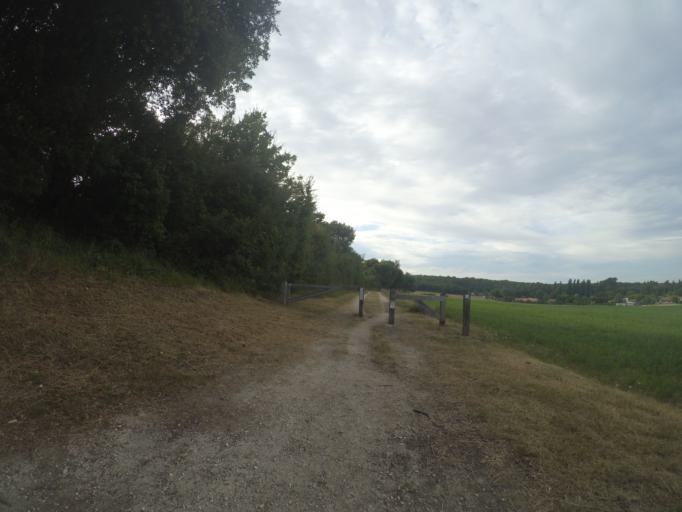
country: FR
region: Poitou-Charentes
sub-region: Departement de la Charente-Maritime
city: Meschers-sur-Gironde
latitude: 45.5745
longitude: -0.9703
